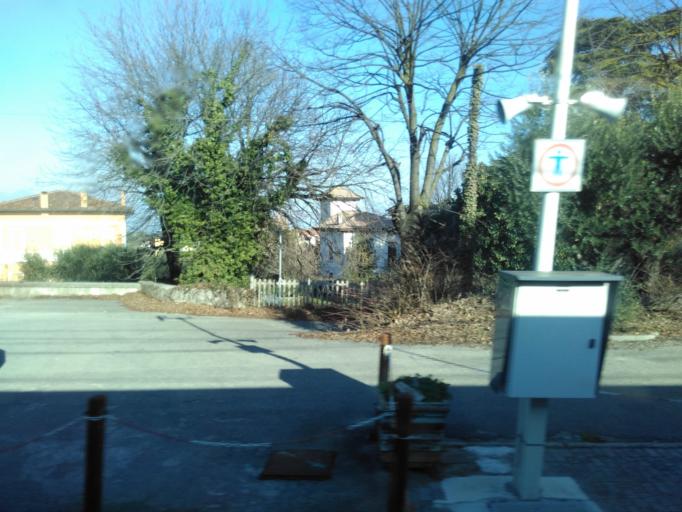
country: IT
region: Lombardy
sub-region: Provincia di Brescia
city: Desenzano del Garda
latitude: 45.4632
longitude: 10.5350
